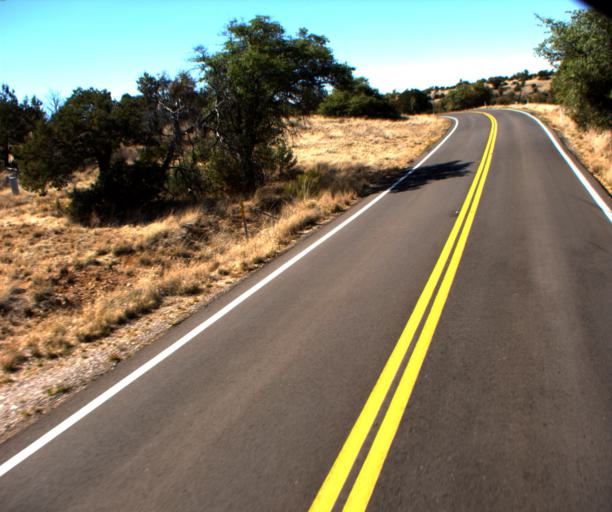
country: US
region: Arizona
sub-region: Cochise County
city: Huachuca City
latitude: 31.5634
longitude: -110.5552
